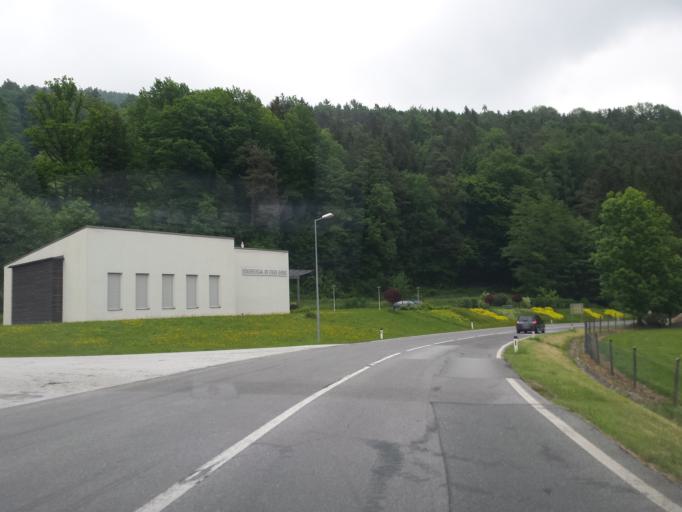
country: AT
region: Styria
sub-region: Politischer Bezirk Weiz
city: Baierdorf-Umgebung
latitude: 47.2601
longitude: 15.7147
